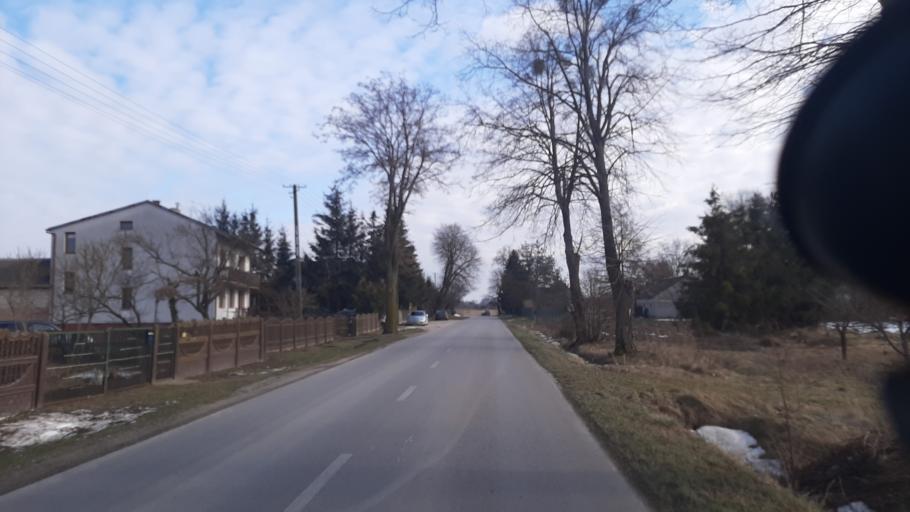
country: PL
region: Lublin Voivodeship
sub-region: Powiat lubartowski
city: Uscimow Stary
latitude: 51.4791
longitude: 22.9192
